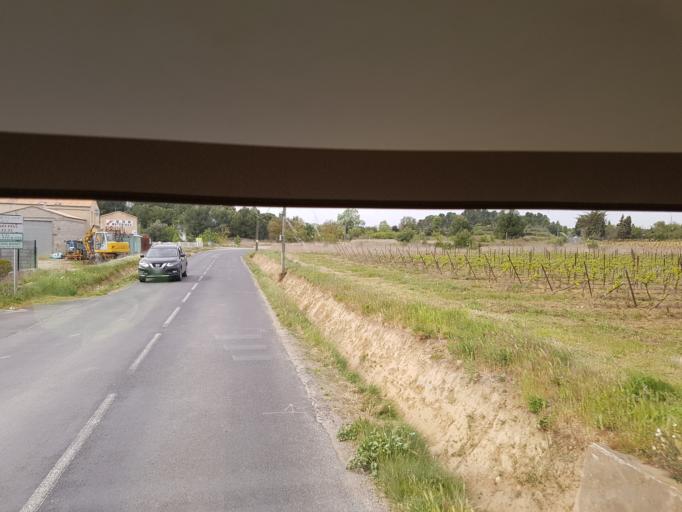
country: FR
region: Languedoc-Roussillon
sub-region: Departement de l'Aude
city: Fleury
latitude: 43.2209
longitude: 3.1327
